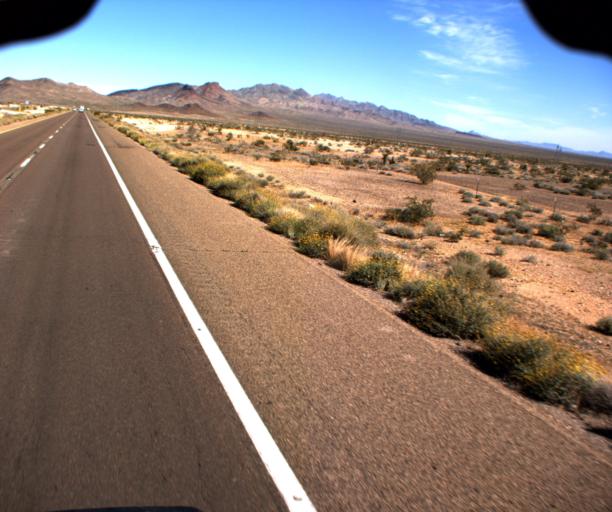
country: US
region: Nevada
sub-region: Clark County
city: Boulder City
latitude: 35.8247
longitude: -114.5565
